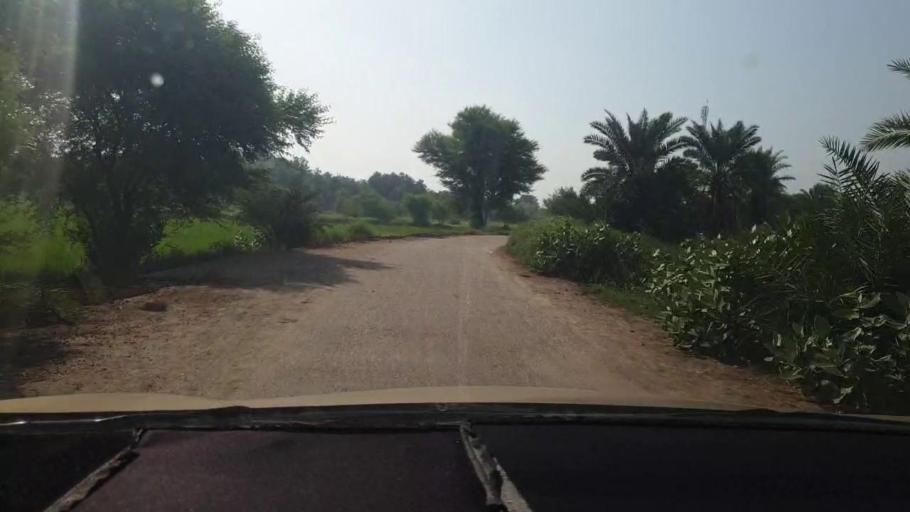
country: PK
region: Sindh
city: Kambar
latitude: 27.6099
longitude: 68.0918
